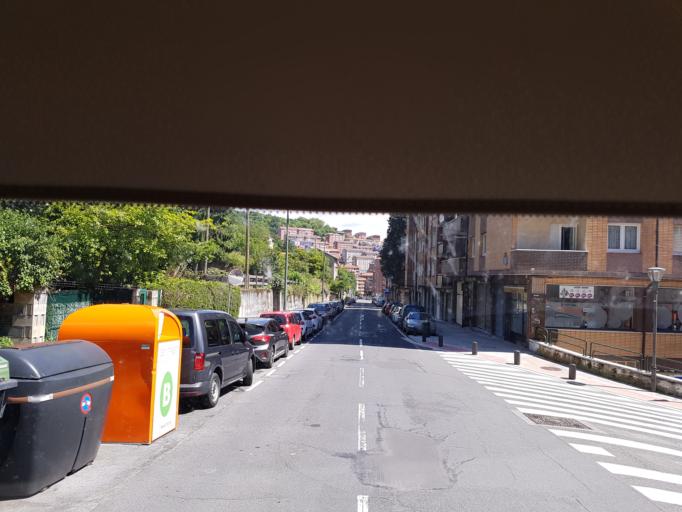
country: ES
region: Basque Country
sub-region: Bizkaia
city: Bilbao
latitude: 43.2688
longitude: -2.9163
